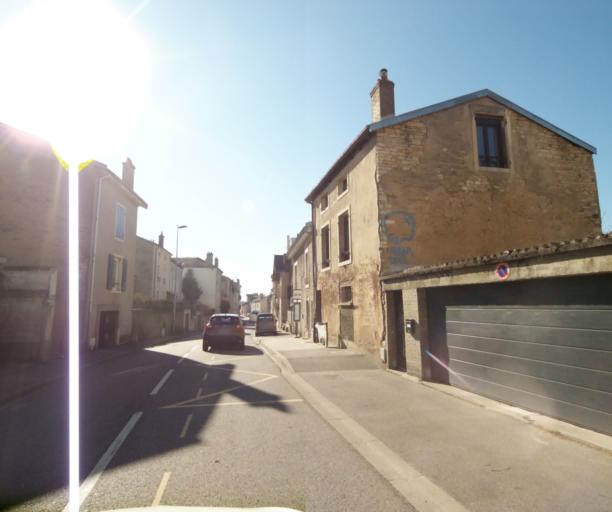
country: FR
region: Lorraine
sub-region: Departement de Meurthe-et-Moselle
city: Malzeville
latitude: 48.7129
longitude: 6.1844
